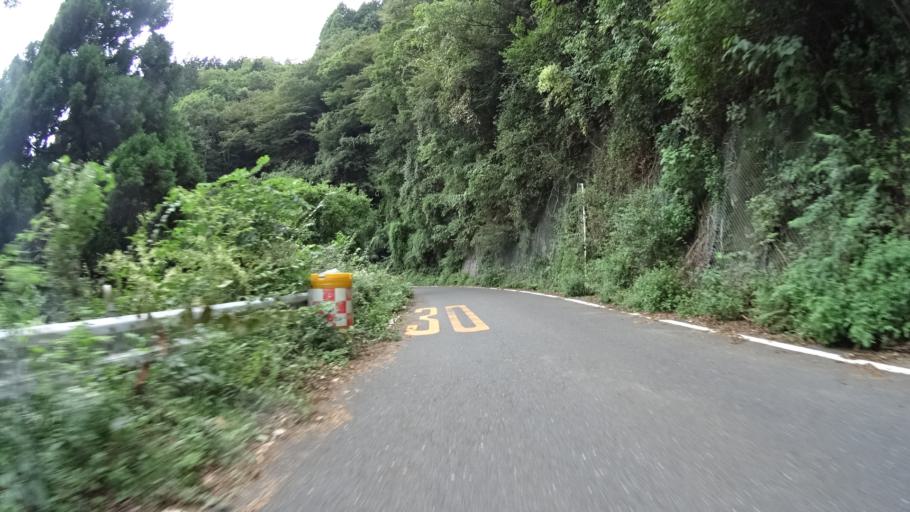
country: JP
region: Kanagawa
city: Hadano
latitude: 35.4271
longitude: 139.2217
